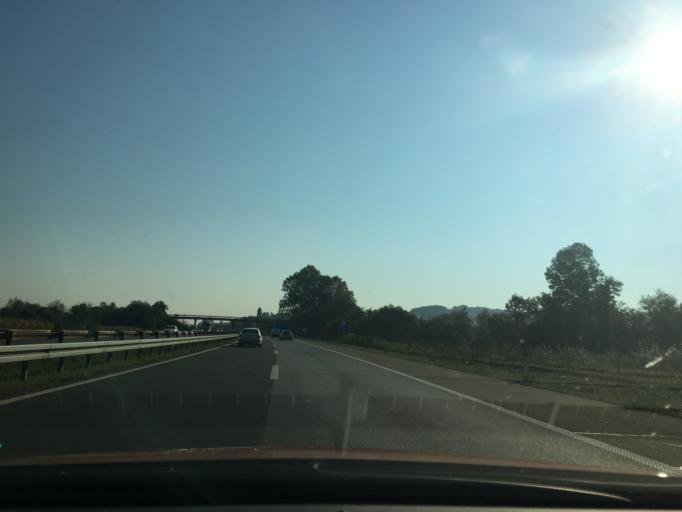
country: RS
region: Central Serbia
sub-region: Belgrade
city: Grocka
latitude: 44.5665
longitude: 20.6904
